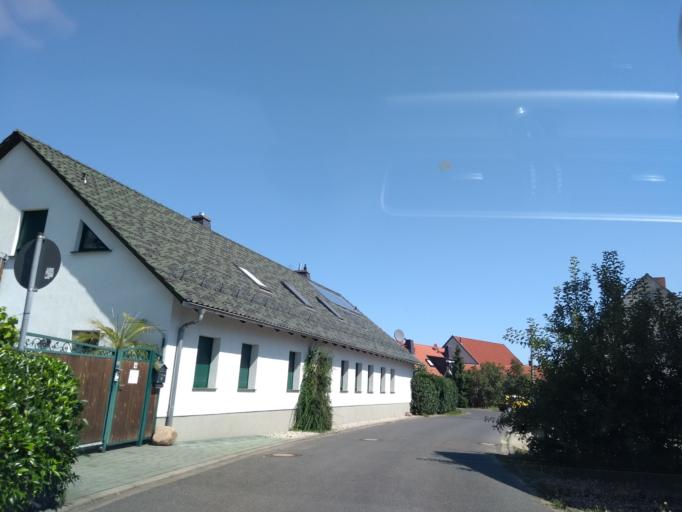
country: DE
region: Brandenburg
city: Lubbenau
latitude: 51.8679
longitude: 13.9606
